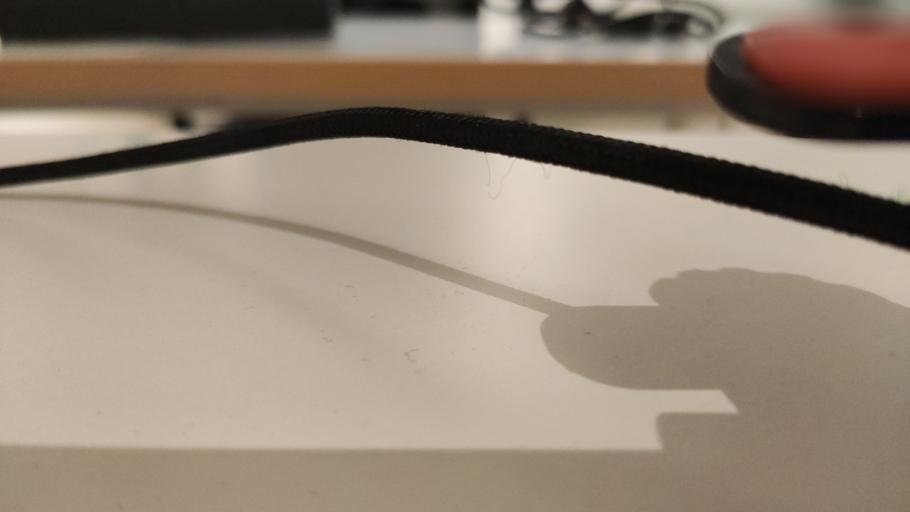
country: RU
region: Moskovskaya
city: Dorokhovo
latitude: 55.5143
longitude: 36.3497
